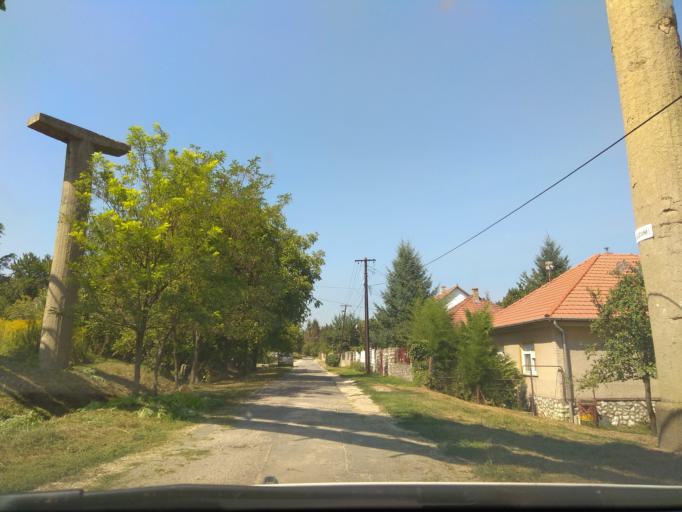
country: HU
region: Borsod-Abauj-Zemplen
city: Miskolc
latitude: 48.0652
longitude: 20.7785
